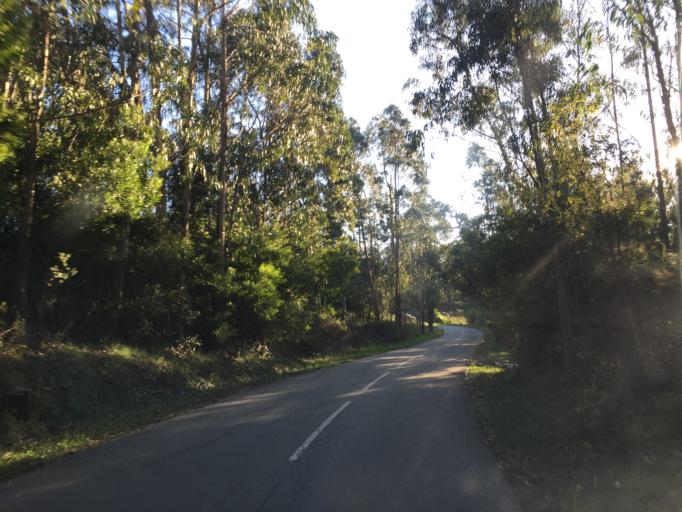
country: PT
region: Coimbra
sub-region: Figueira da Foz
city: Alhadas
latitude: 40.1601
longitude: -8.8004
